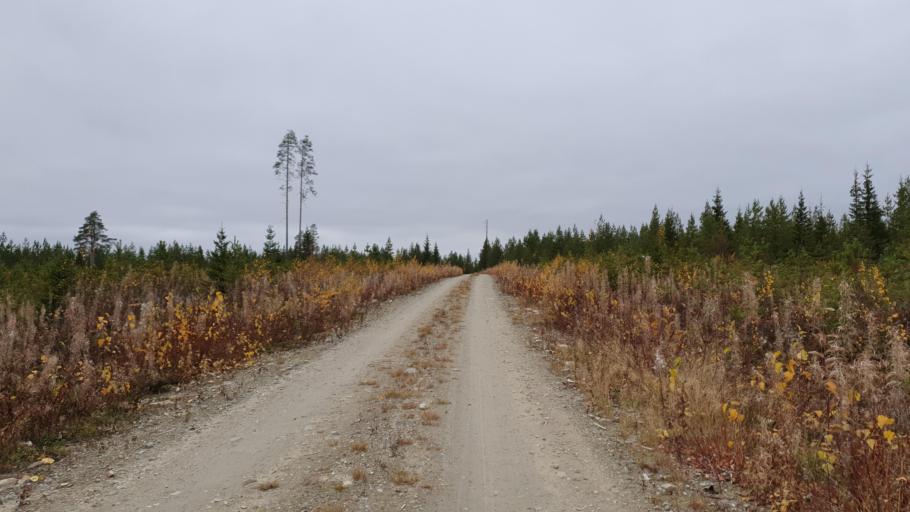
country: FI
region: Kainuu
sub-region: Kehys-Kainuu
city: Kuhmo
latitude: 64.4470
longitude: 29.6200
